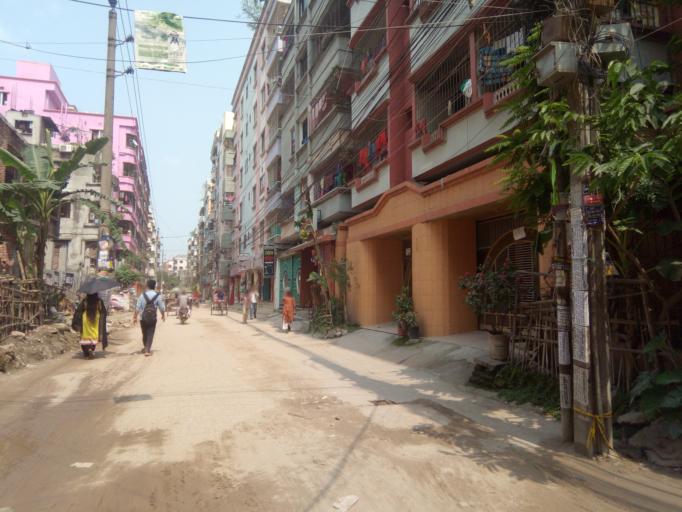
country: BD
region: Dhaka
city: Paltan
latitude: 23.7613
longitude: 90.4340
